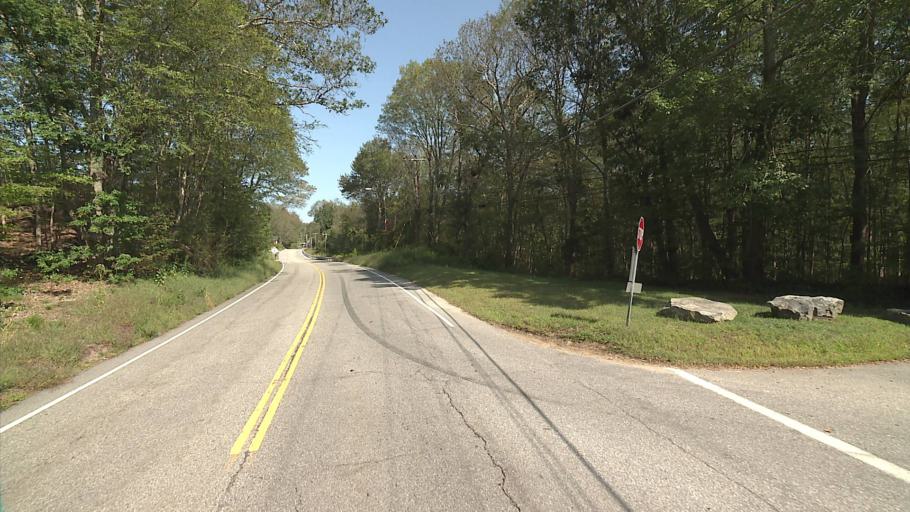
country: US
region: Connecticut
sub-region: Windham County
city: East Brooklyn
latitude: 41.7975
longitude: -71.9482
